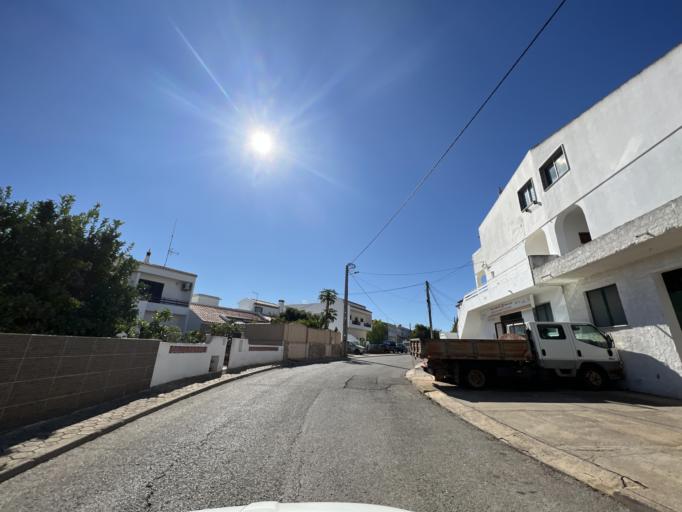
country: PT
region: Faro
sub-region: Lagoa
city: Estombar
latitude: 37.1445
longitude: -8.5103
